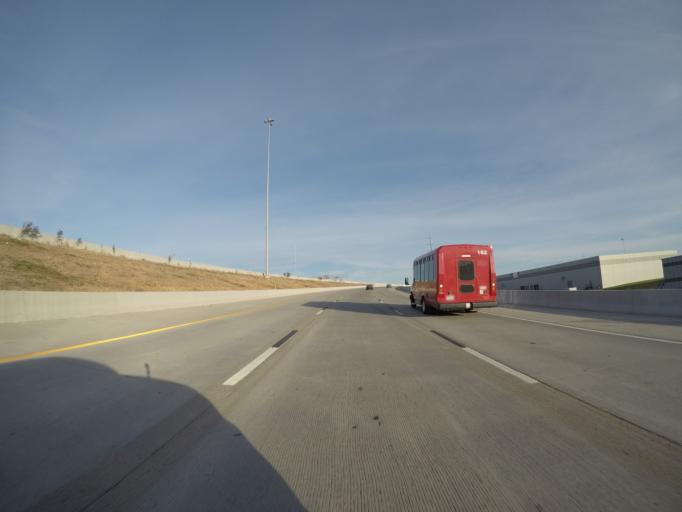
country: US
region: Kansas
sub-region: Johnson County
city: Lenexa
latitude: 38.9418
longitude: -94.7554
